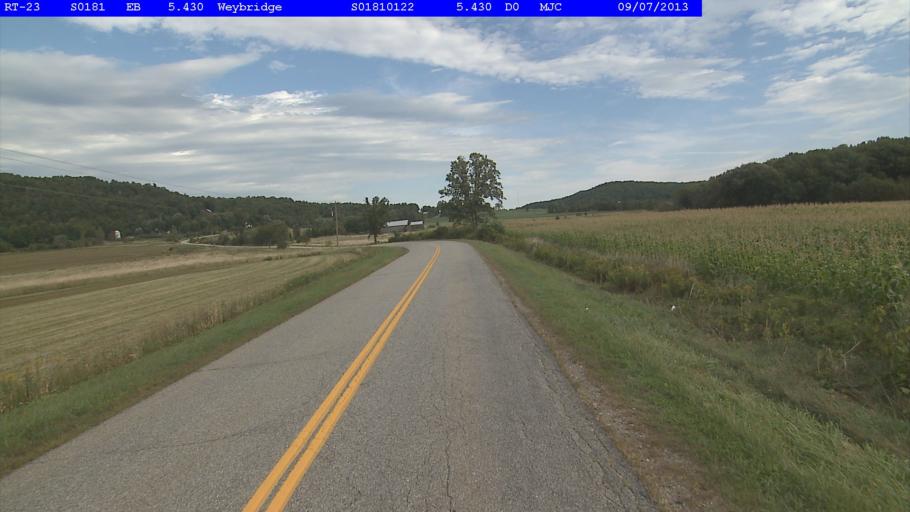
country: US
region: Vermont
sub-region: Addison County
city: Middlebury (village)
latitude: 44.0692
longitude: -73.2503
